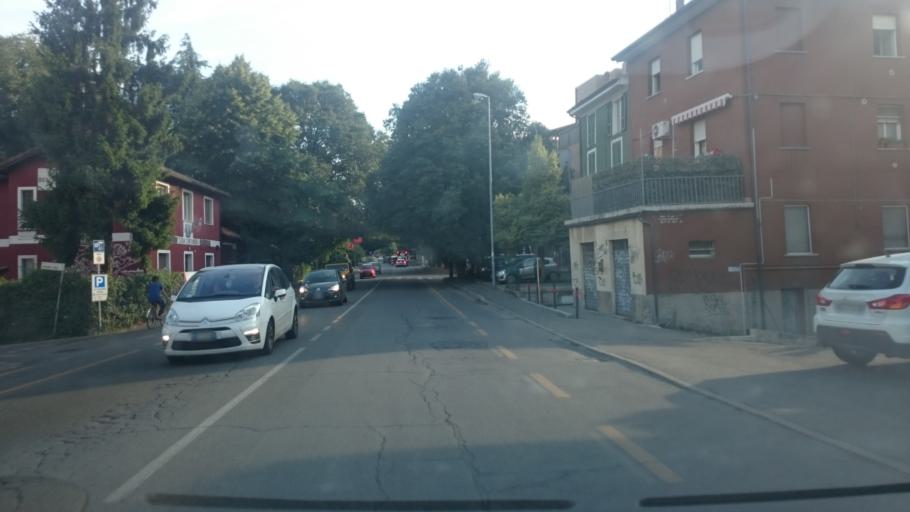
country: IT
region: Emilia-Romagna
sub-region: Provincia di Reggio Emilia
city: Reggio nell'Emilia
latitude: 44.6832
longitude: 10.6221
